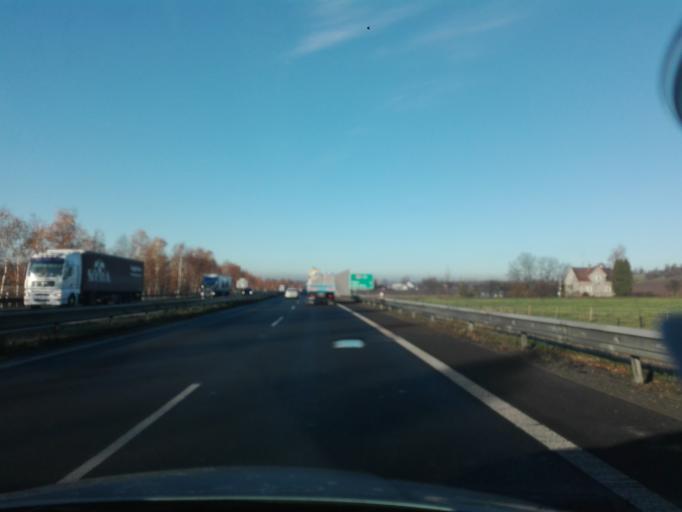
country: CZ
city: Dobra
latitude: 49.6755
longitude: 18.4212
